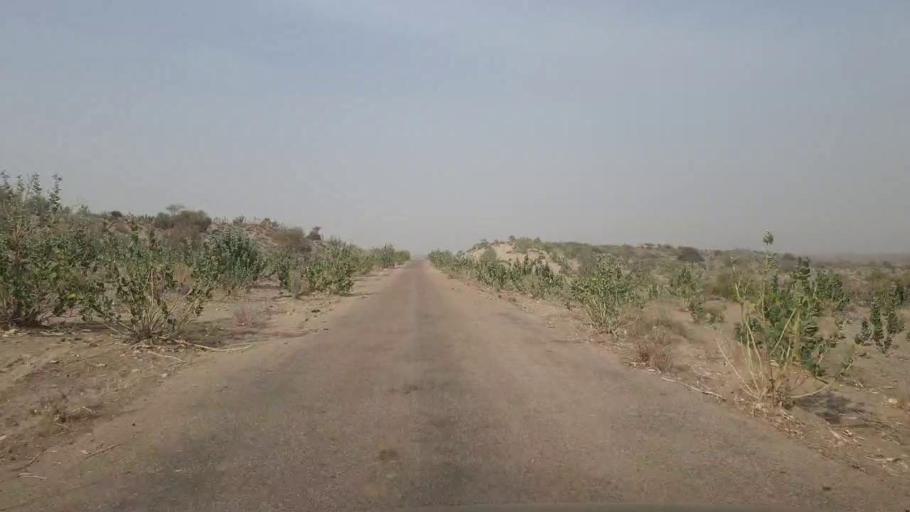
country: PK
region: Sindh
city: Chor
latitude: 25.6282
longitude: 69.9291
